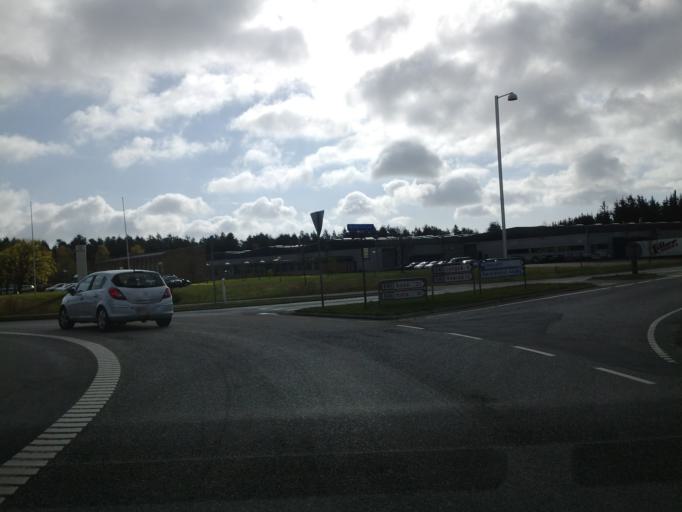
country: DK
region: North Denmark
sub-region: Frederikshavn Kommune
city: Saeby
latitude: 57.3205
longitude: 10.4802
